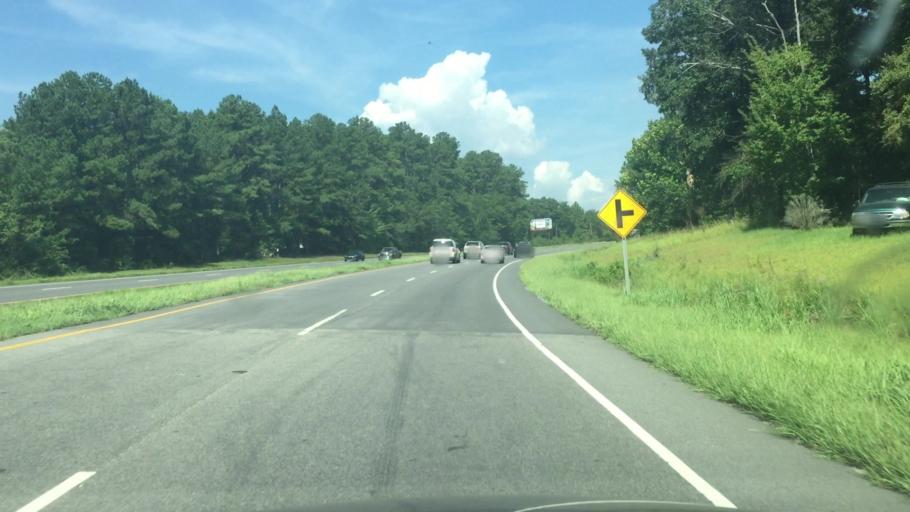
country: US
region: North Carolina
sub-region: Scotland County
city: Laurel Hill
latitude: 34.8000
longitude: -79.5338
